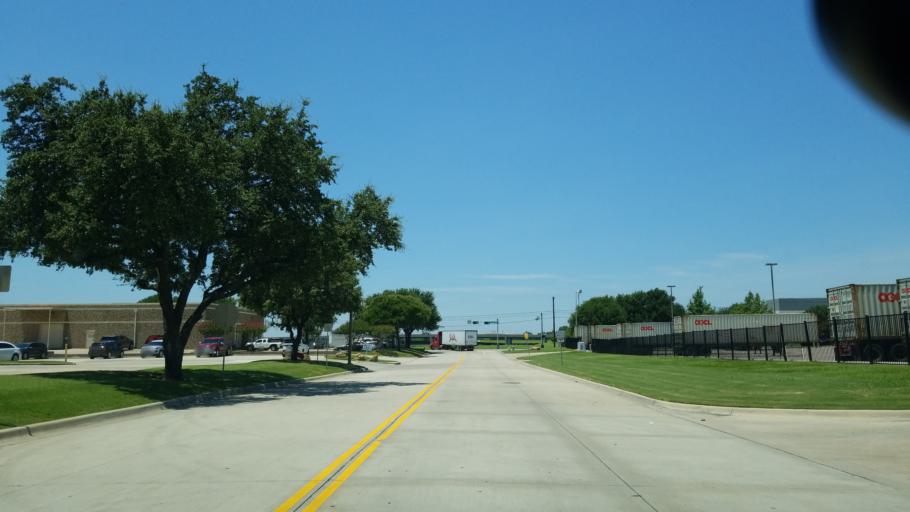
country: US
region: Texas
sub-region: Dallas County
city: Farmers Branch
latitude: 32.9266
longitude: -96.9237
